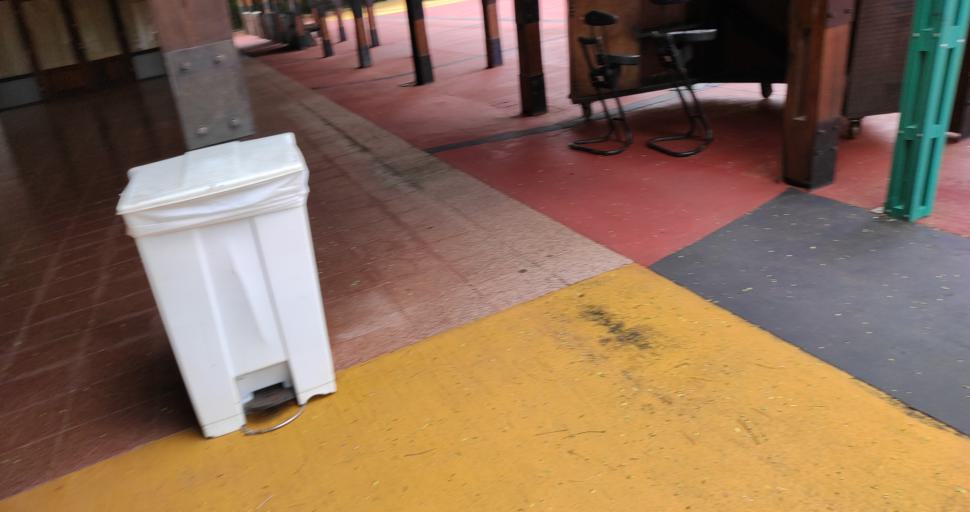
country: AR
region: Misiones
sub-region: Departamento de Iguazu
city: Puerto Iguazu
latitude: -25.6808
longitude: -54.4531
